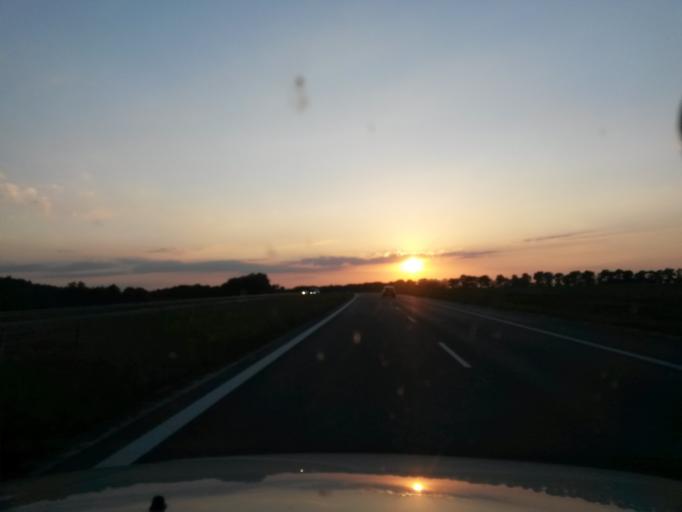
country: PL
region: Lodz Voivodeship
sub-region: Powiat wieruszowski
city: Wieruszow
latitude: 51.3350
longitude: 18.1378
